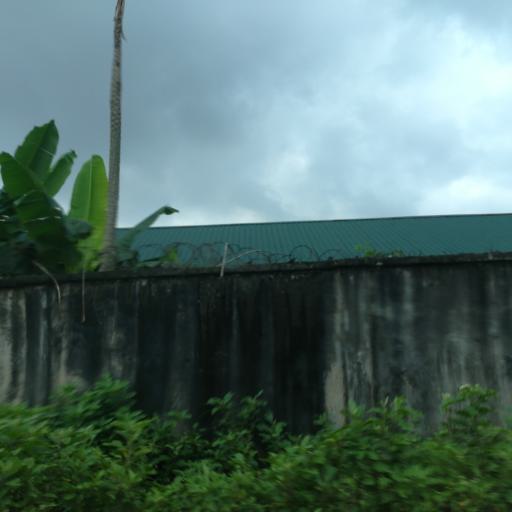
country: NG
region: Rivers
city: Port Harcourt
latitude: 4.8291
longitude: 7.0379
